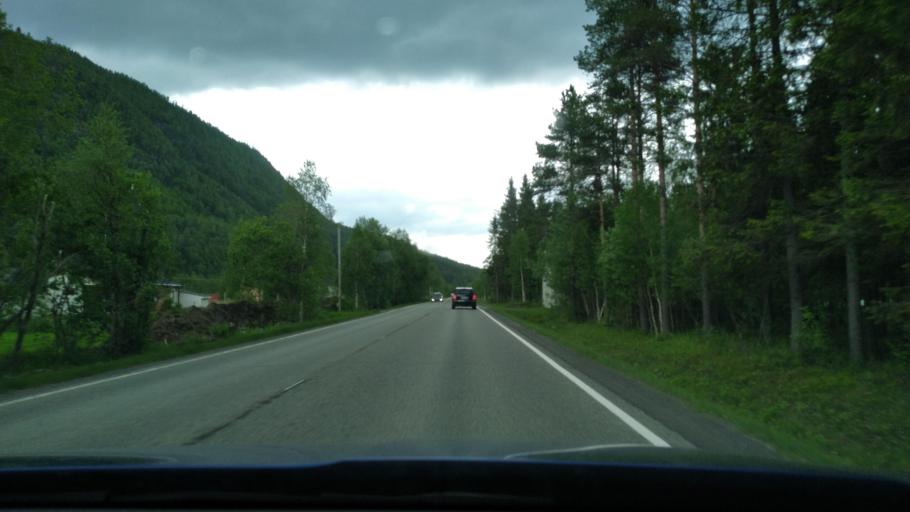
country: NO
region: Troms
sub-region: Bardu
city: Setermoen
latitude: 68.9711
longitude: 18.4925
